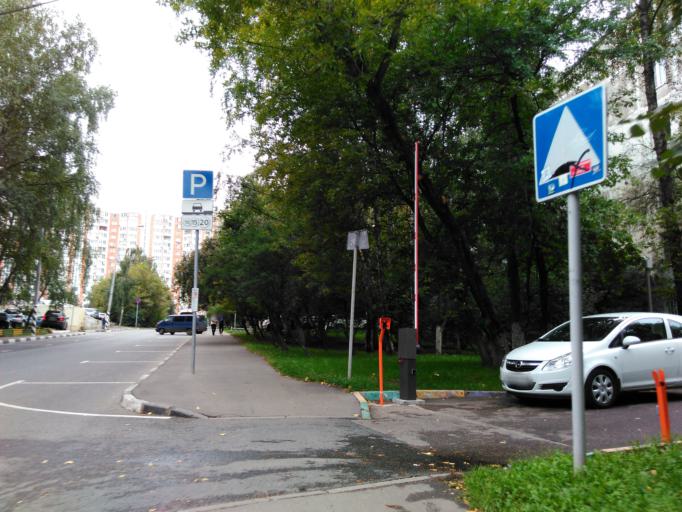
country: RU
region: Moskovskaya
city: Cheremushki
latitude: 55.6741
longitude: 37.5794
